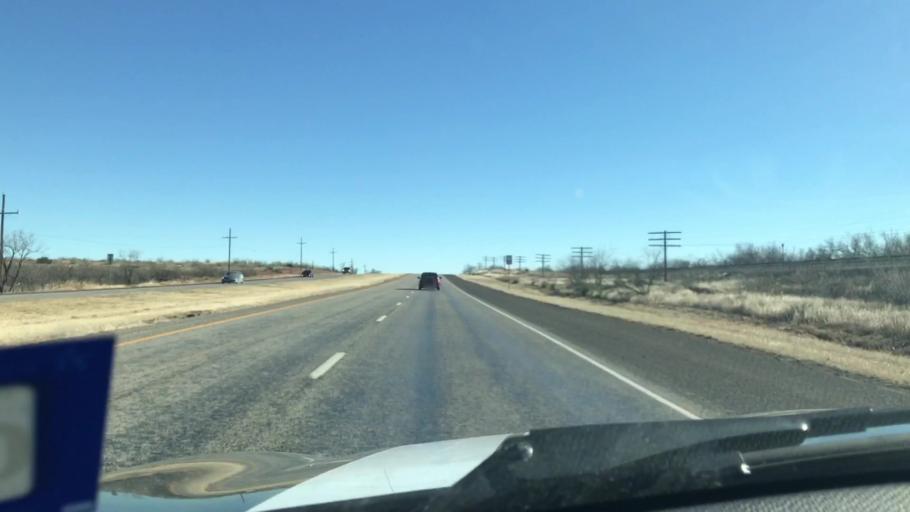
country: US
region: Texas
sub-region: Garza County
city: Post
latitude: 33.0339
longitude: -101.1934
